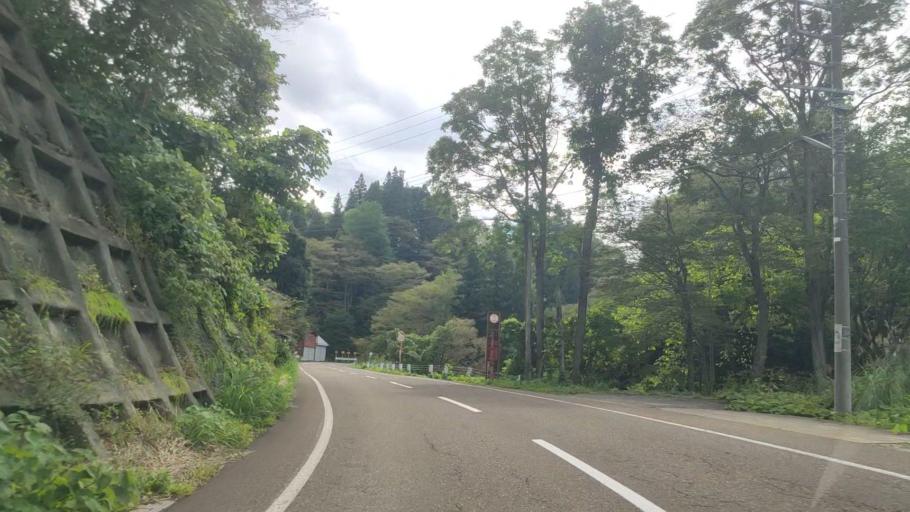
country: JP
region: Niigata
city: Arai
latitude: 36.9317
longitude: 138.2978
